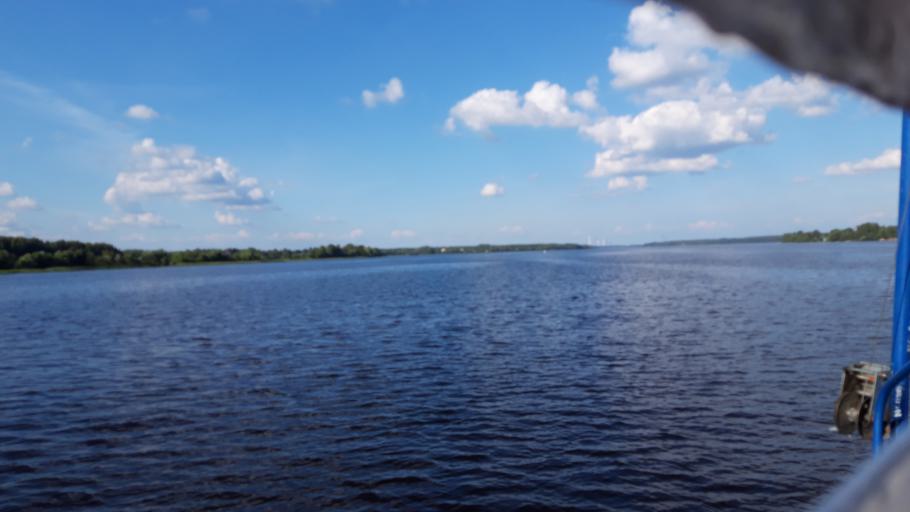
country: RU
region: Tverskaya
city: Konakovo
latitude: 56.6557
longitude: 36.6370
